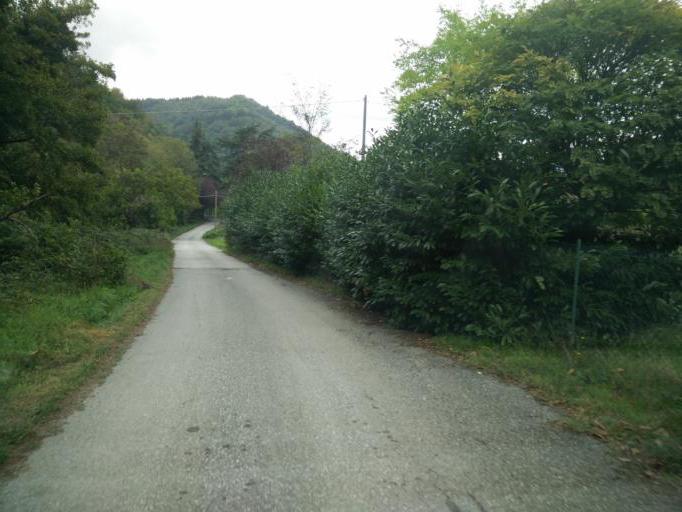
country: IT
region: Tuscany
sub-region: Provincia di Massa-Carrara
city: Casola in Lunigiana
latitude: 44.1993
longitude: 10.1731
